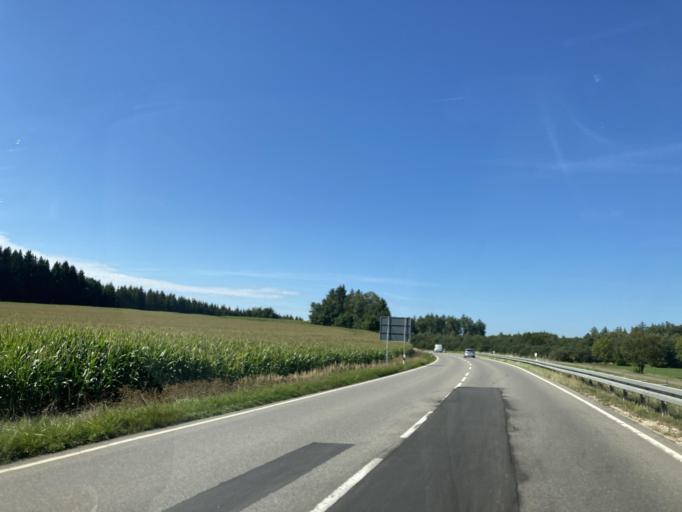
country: DE
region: Baden-Wuerttemberg
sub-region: Tuebingen Region
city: Uttenweiler
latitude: 48.1434
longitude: 9.5858
